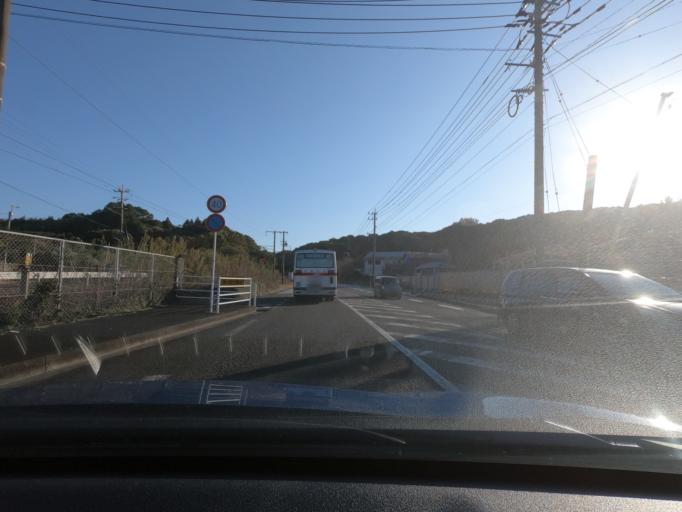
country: JP
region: Kagoshima
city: Akune
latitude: 32.0006
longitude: 130.1960
